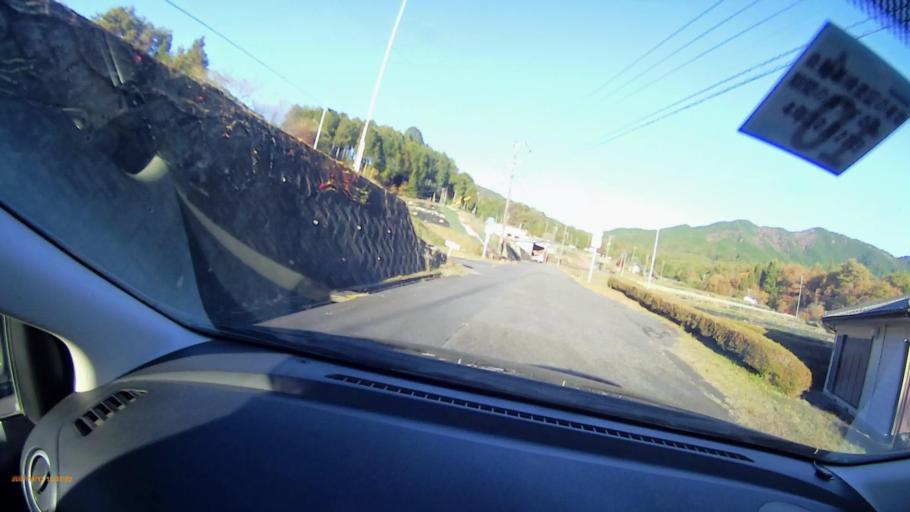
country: JP
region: Gifu
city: Nakatsugawa
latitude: 35.5814
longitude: 137.3743
